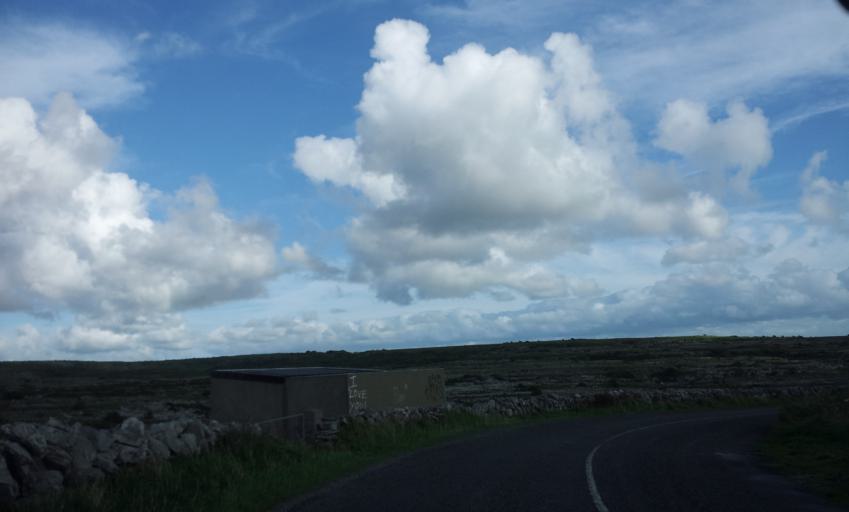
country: IE
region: Connaught
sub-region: County Galway
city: Bearna
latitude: 53.0594
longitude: -9.1473
